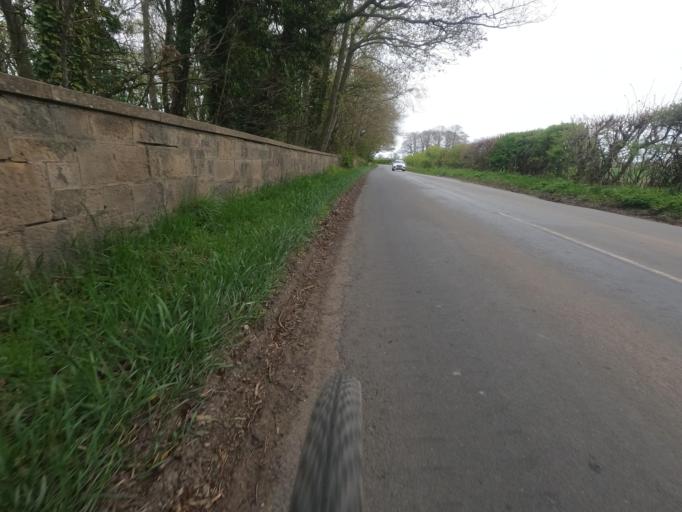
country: GB
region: England
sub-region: Northumberland
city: Ponteland
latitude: 55.0845
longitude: -1.7624
